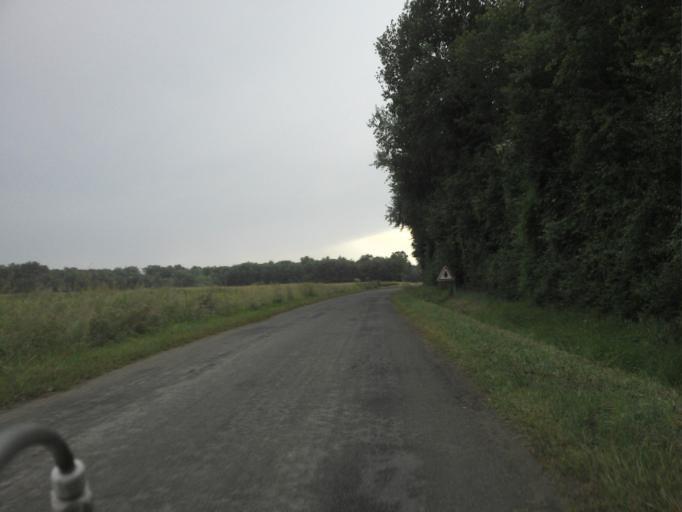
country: FR
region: Pays de la Loire
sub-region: Departement de Maine-et-Loire
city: Breze
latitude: 47.1036
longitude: -0.0049
